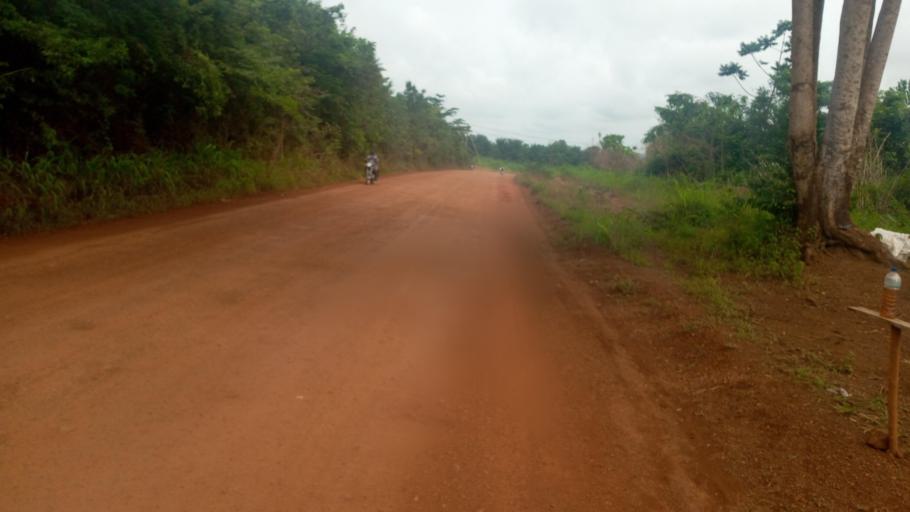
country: SL
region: Southern Province
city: Mogbwemo
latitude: 7.7406
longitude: -12.2873
